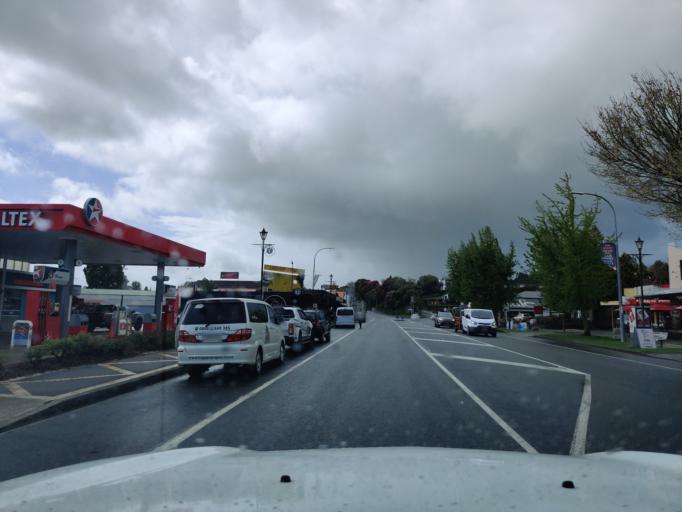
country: NZ
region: Waikato
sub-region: Matamata-Piako District
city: Matamata
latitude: -37.9775
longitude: 175.7567
